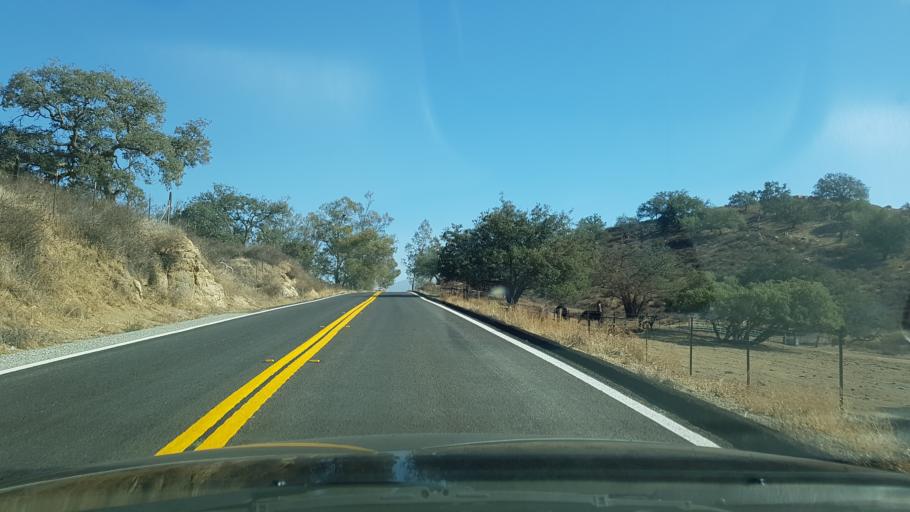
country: US
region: California
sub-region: San Diego County
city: San Diego Country Estates
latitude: 33.0701
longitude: -116.7641
